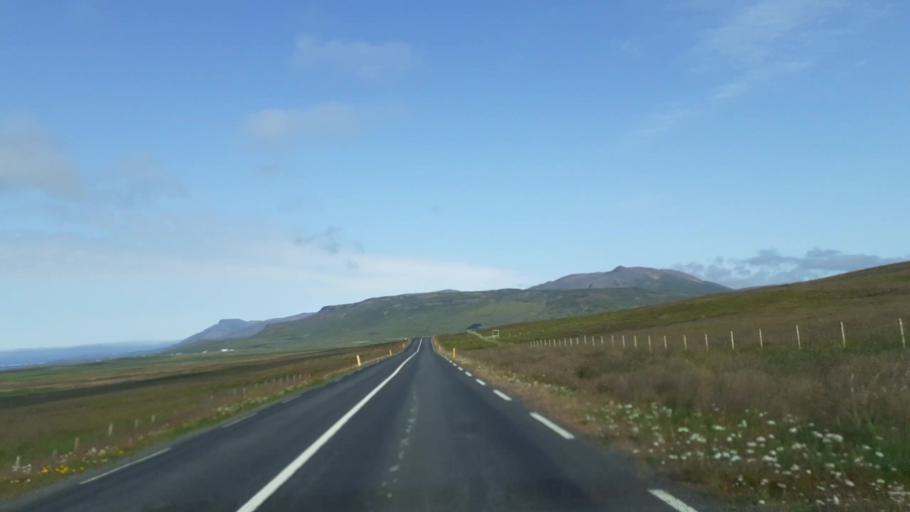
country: IS
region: Northwest
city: Saudarkrokur
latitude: 65.7031
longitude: -20.2354
